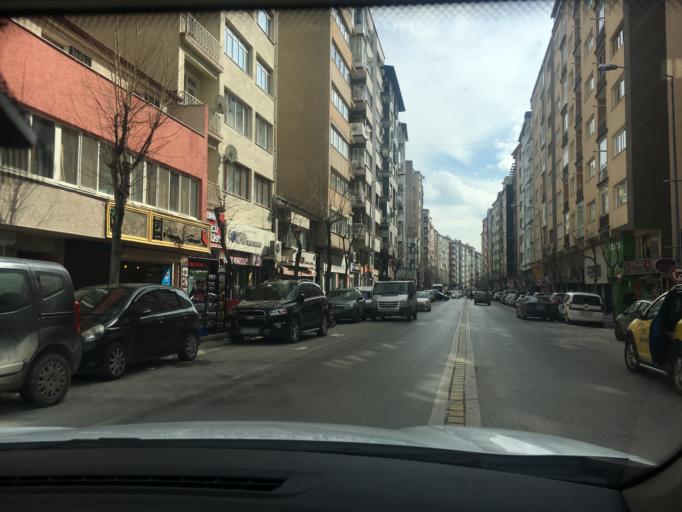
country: TR
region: Eskisehir
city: Eskisehir
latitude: 39.7806
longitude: 30.5144
